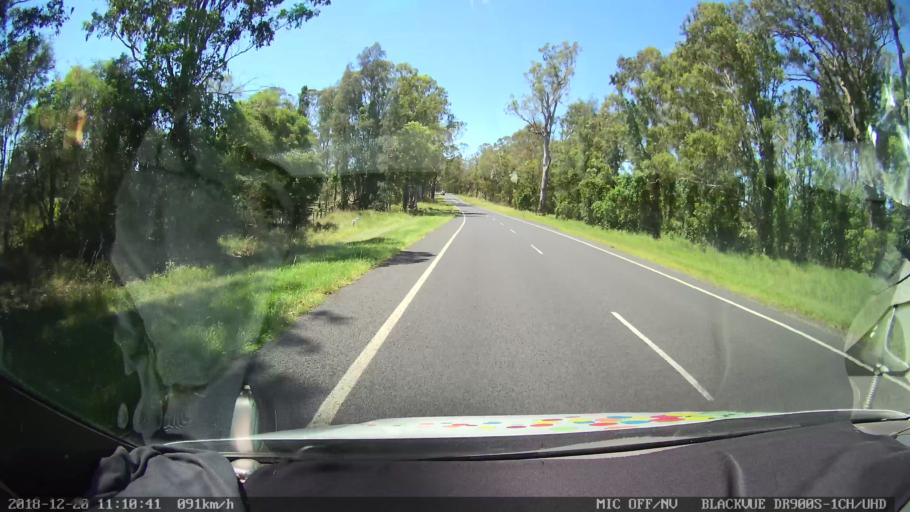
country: AU
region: New South Wales
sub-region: Richmond Valley
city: Casino
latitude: -28.9524
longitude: 153.0101
